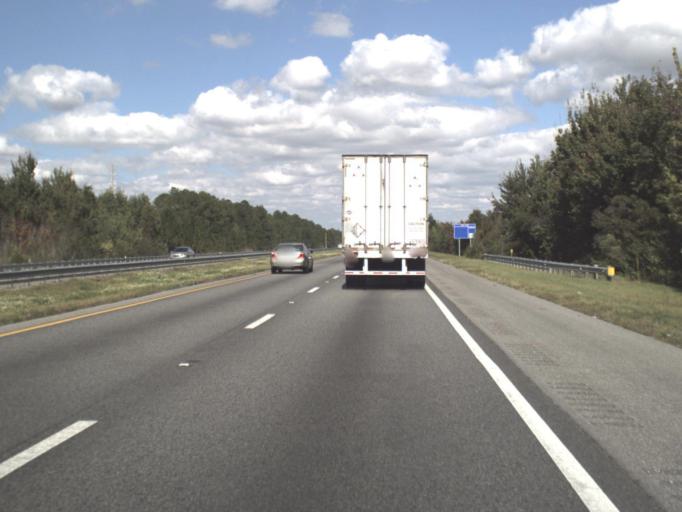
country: US
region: Florida
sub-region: Osceola County
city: Buenaventura Lakes
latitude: 28.3194
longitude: -81.3716
